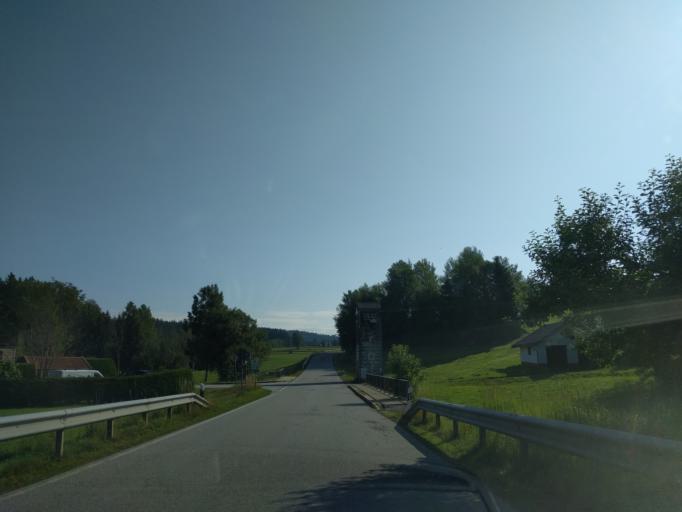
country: DE
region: Bavaria
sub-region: Lower Bavaria
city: Mauth
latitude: 48.8647
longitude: 13.5389
